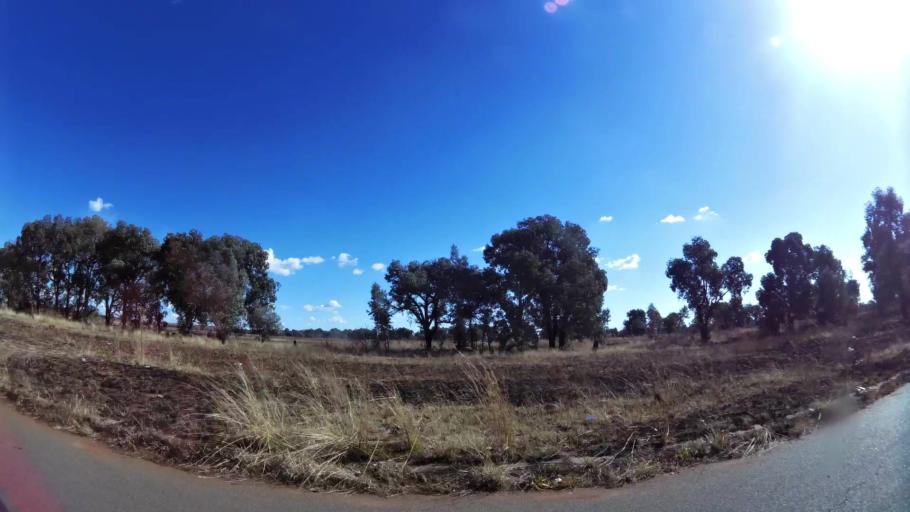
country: ZA
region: Gauteng
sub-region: West Rand District Municipality
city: Carletonville
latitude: -26.3700
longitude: 27.3783
